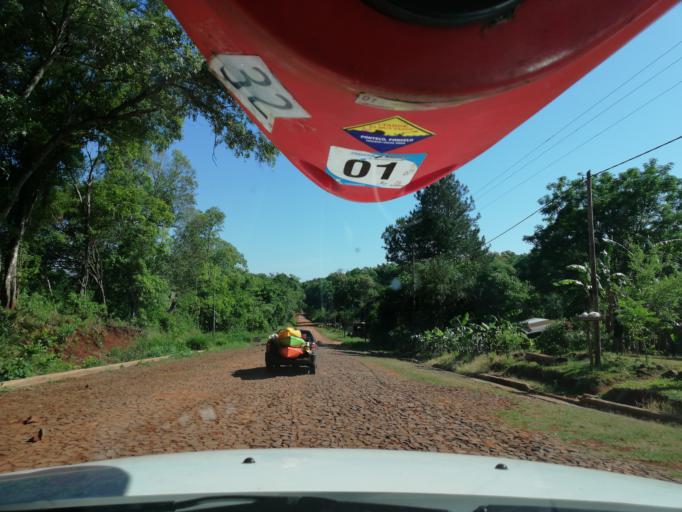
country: AR
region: Misiones
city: Puerto Leoni
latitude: -26.9810
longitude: -55.1648
